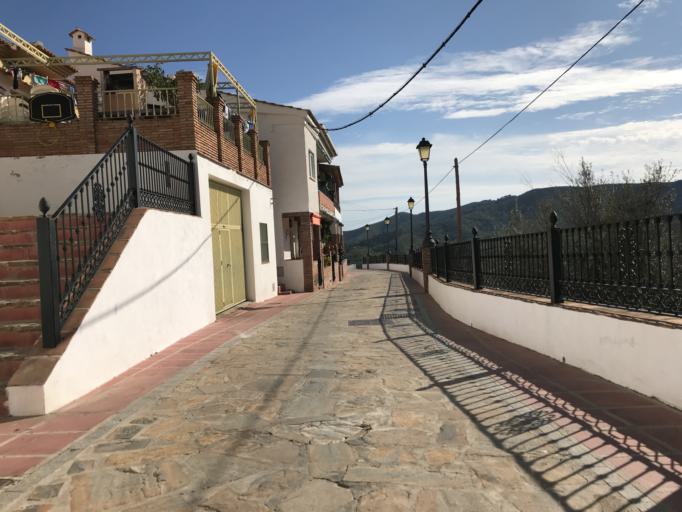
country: ES
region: Andalusia
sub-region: Provincia de Malaga
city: Valdes
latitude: 36.7701
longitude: -4.2167
